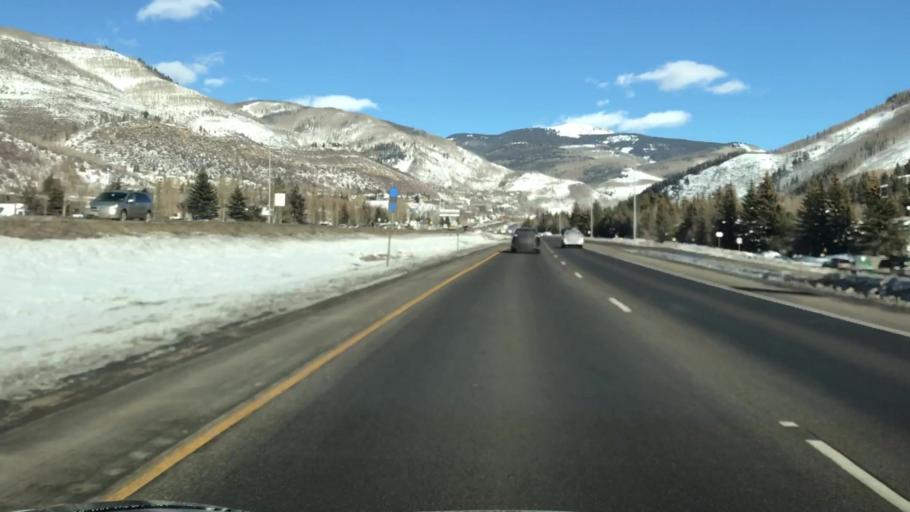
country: US
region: Colorado
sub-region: Eagle County
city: Minturn
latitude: 39.6286
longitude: -106.4194
